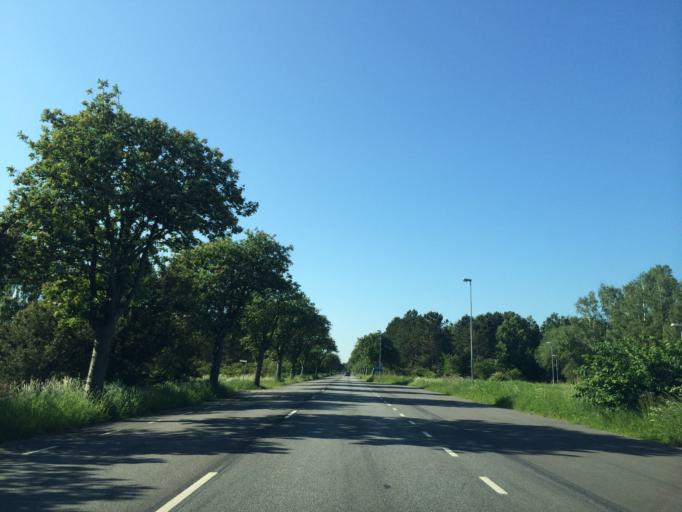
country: SE
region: Skane
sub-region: Lomma Kommun
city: Lomma
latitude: 55.6863
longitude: 13.0633
